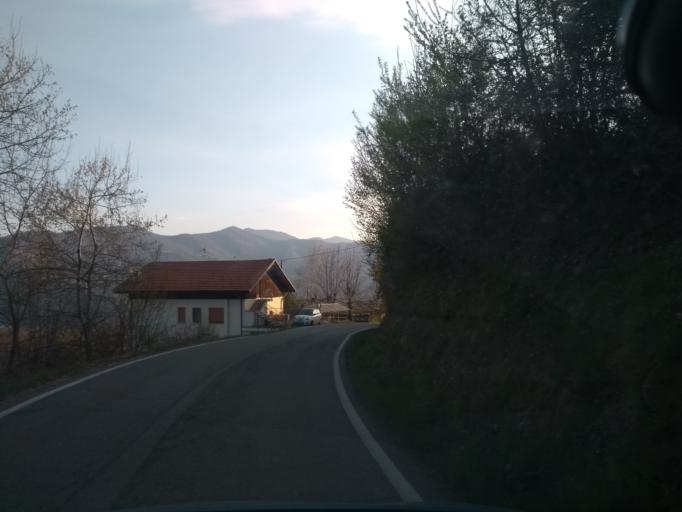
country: IT
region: Piedmont
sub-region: Provincia di Torino
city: Lanzo Torinese
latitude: 45.2916
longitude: 7.4820
